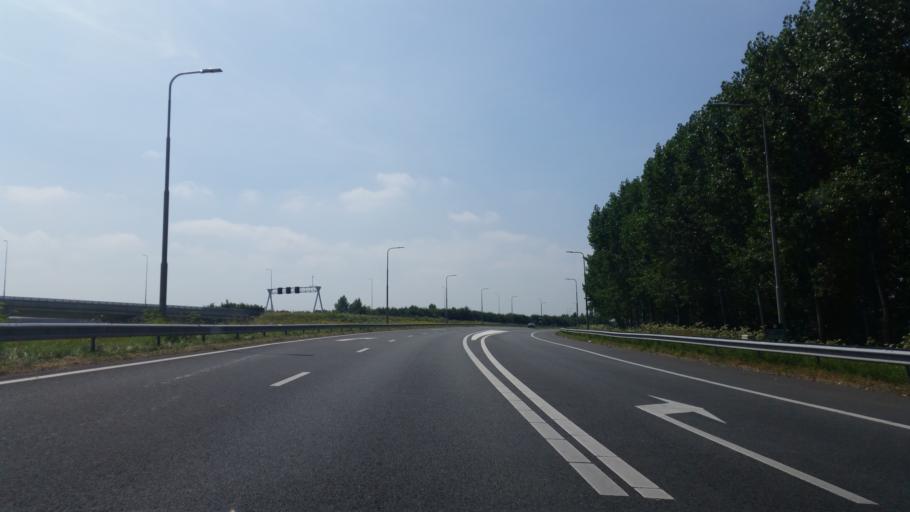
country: NL
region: South Holland
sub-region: Gemeente Ridderkerk
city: Ridderkerk
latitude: 51.8758
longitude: 4.5665
